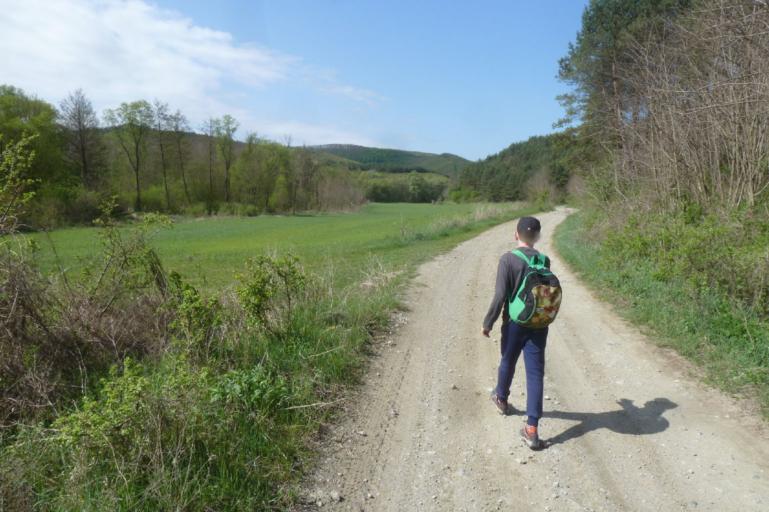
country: HU
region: Nograd
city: Matranovak
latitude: 48.0885
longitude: 20.0165
